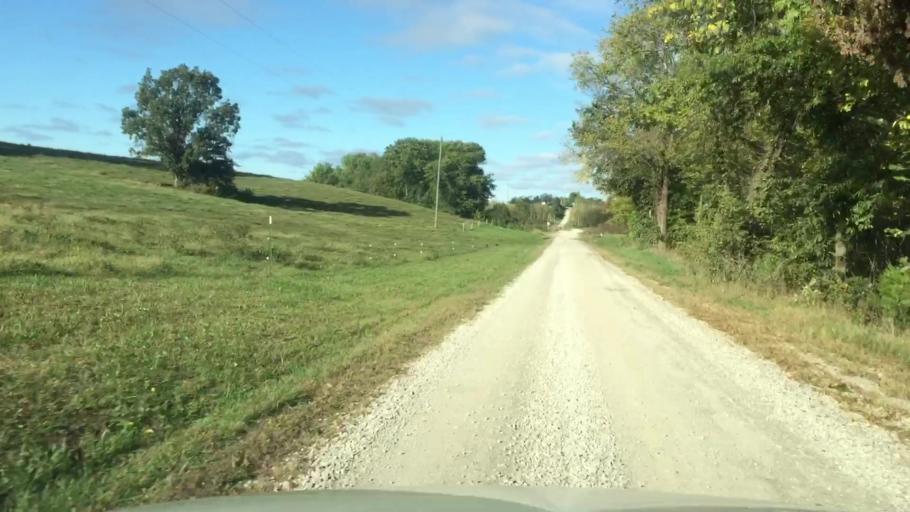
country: US
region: Missouri
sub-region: Howard County
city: New Franklin
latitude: 39.0832
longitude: -92.7635
